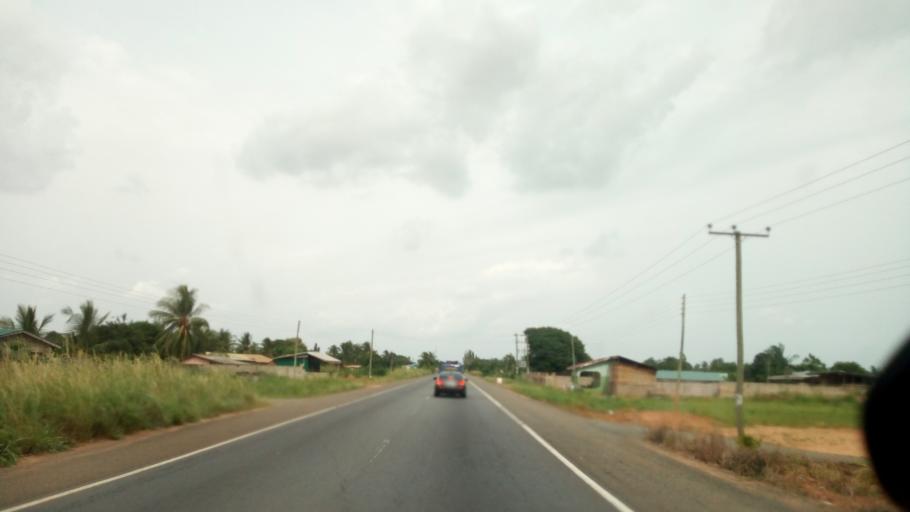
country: GH
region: Volta
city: Keta
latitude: 6.0648
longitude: 0.9009
